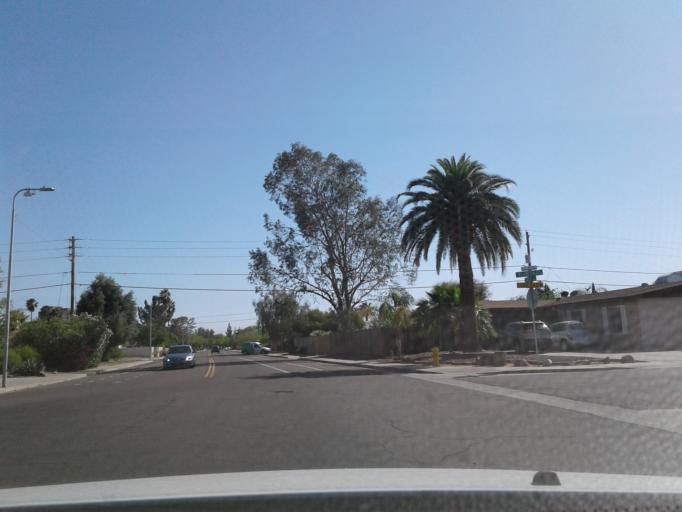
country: US
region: Arizona
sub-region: Maricopa County
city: Tempe
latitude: 33.3992
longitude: -111.9162
